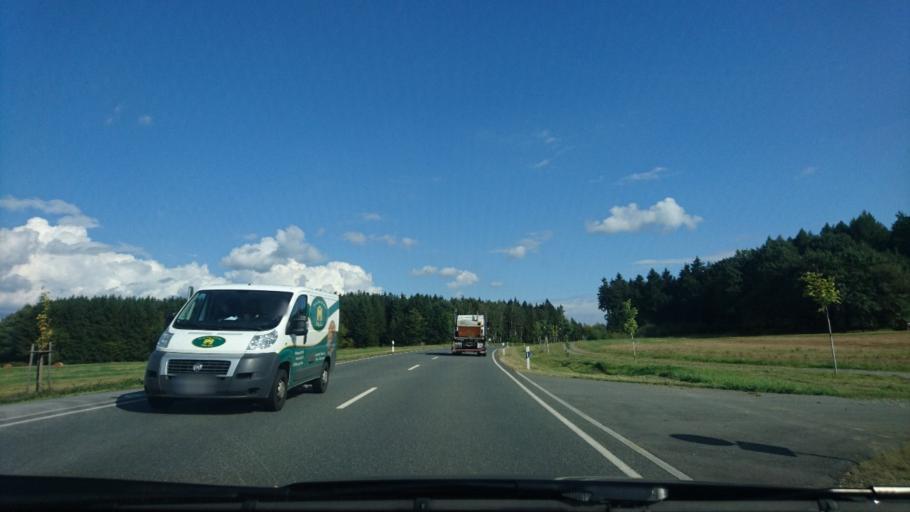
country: DE
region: Saxony
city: Lengenfeld
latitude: 50.5423
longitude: 12.3592
